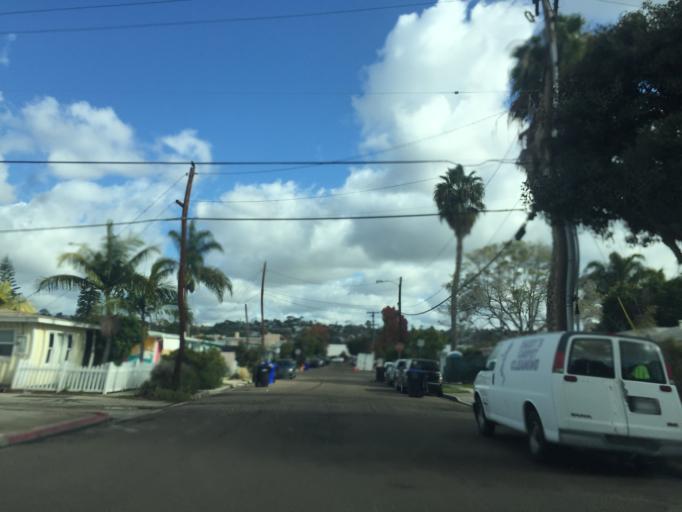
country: US
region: California
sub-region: San Diego County
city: La Jolla
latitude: 32.8031
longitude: -117.2211
